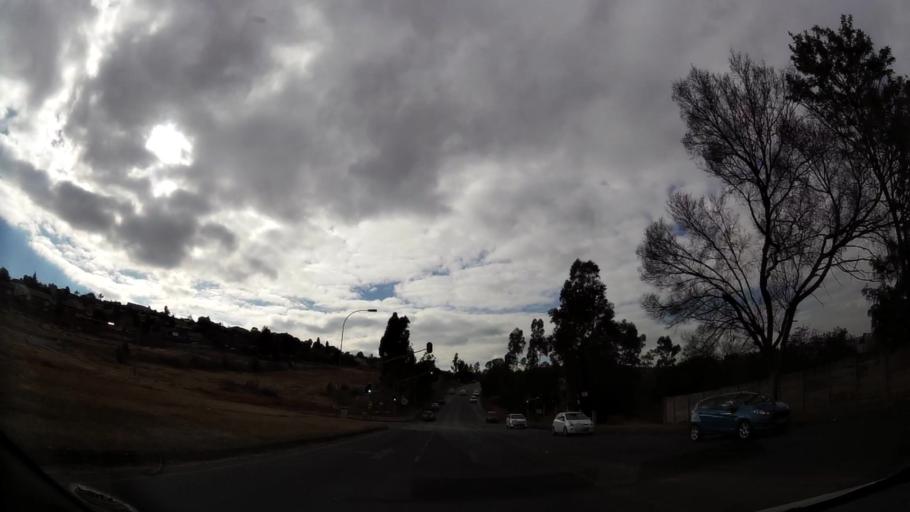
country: ZA
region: Gauteng
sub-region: City of Johannesburg Metropolitan Municipality
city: Roodepoort
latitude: -26.1075
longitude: 27.8585
